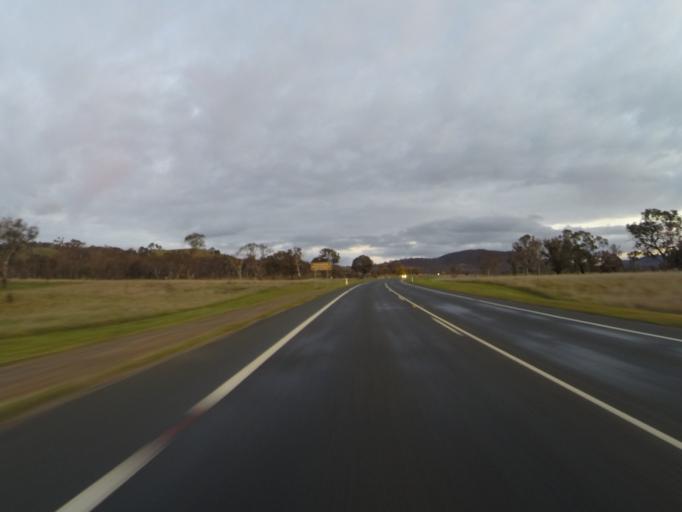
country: AU
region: Australian Capital Territory
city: Kaleen
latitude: -35.2033
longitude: 149.1688
